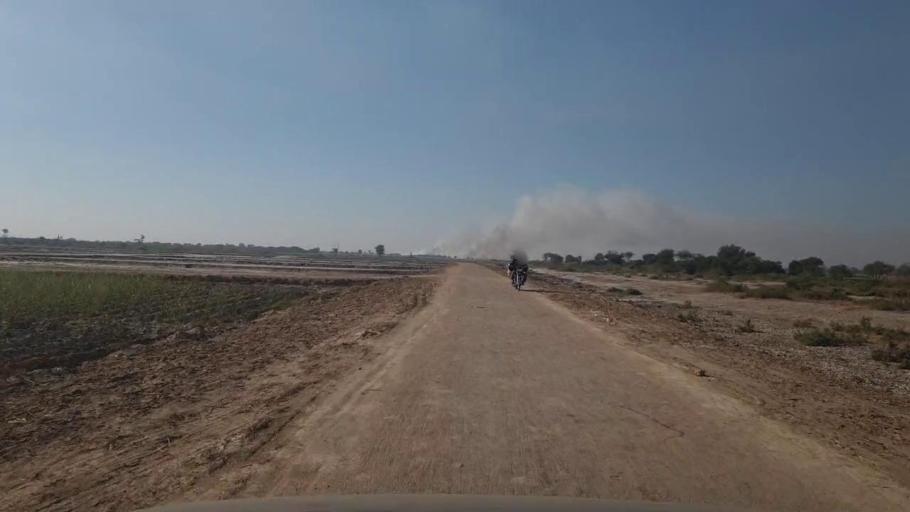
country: PK
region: Sindh
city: Mirwah Gorchani
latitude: 25.3023
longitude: 69.0889
